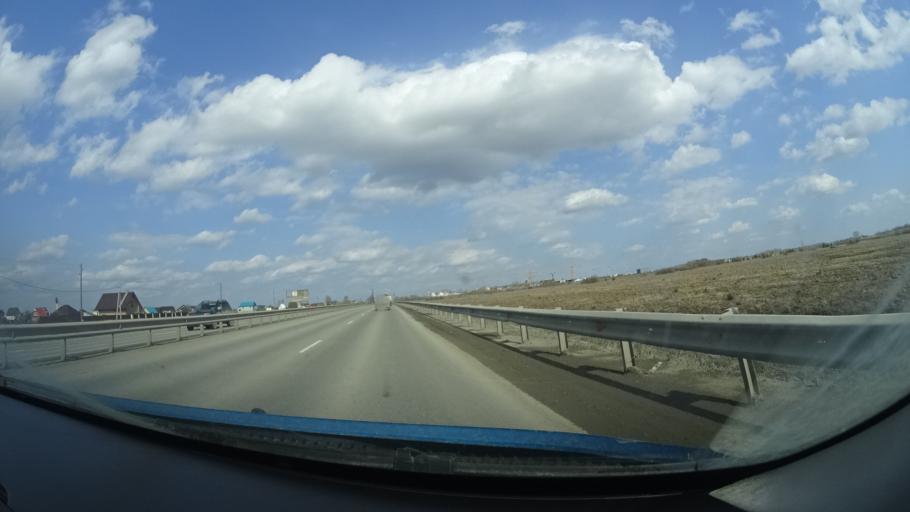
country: RU
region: Perm
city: Kultayevo
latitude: 57.9108
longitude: 55.9944
